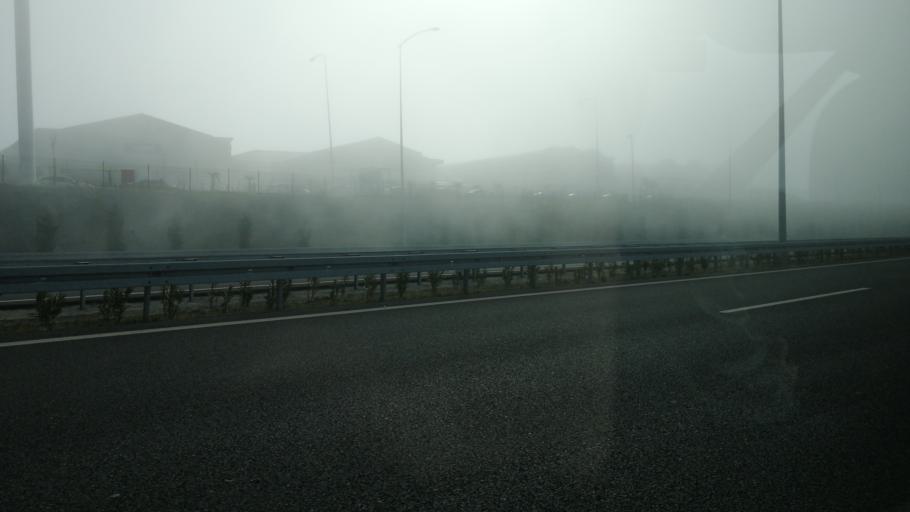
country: TR
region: Kocaeli
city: Tavsanli
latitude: 40.7738
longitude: 29.5184
